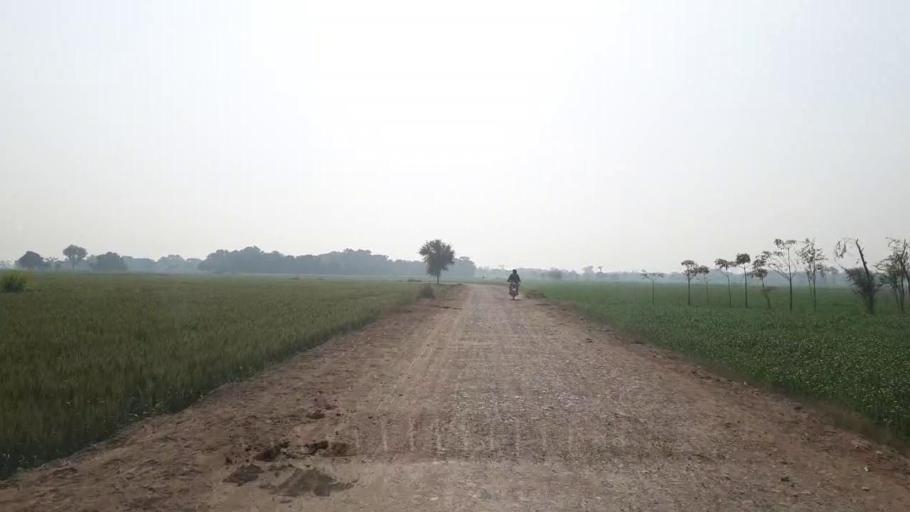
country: PK
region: Sindh
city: Bhit Shah
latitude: 25.7325
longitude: 68.5214
